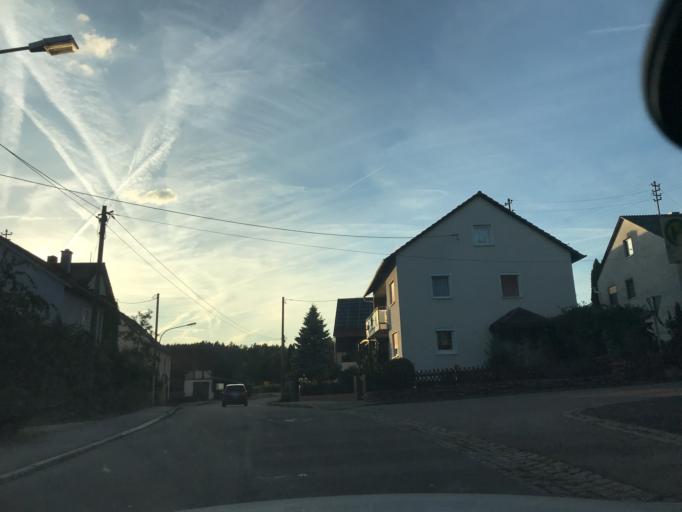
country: DE
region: Bavaria
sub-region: Upper Franconia
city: Pegnitz
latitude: 49.7266
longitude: 11.5606
